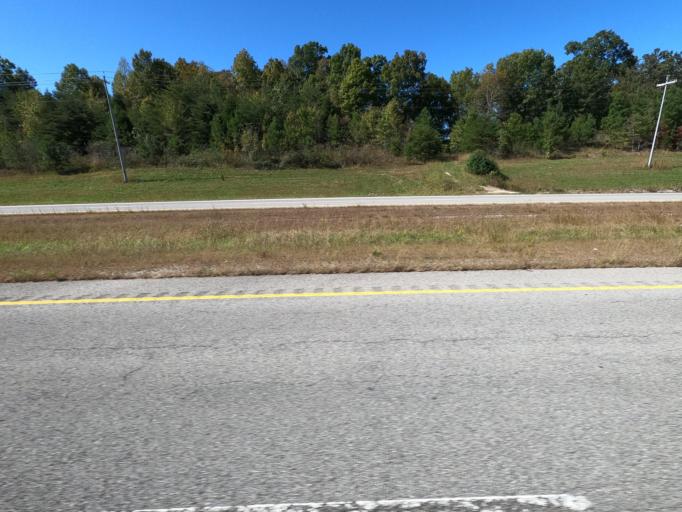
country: US
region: Tennessee
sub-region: Maury County
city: Mount Pleasant
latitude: 35.4651
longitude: -87.2665
